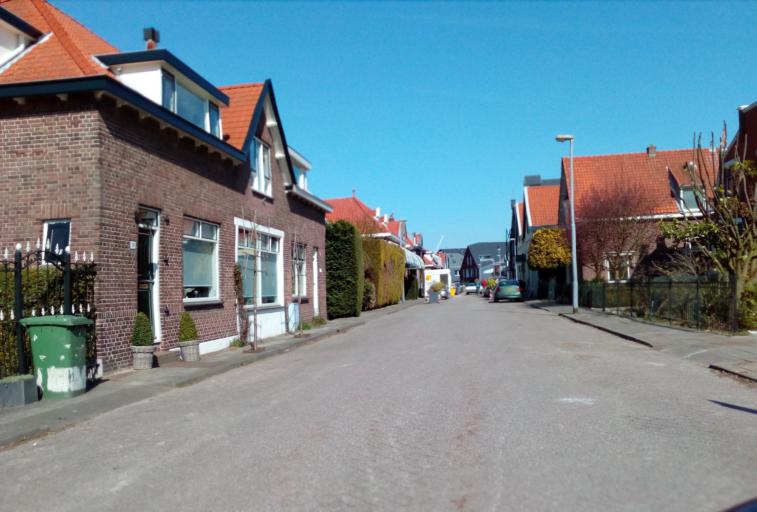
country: NL
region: South Holland
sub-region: Gemeente Lansingerland
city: Bergschenhoek
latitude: 51.9539
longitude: 4.5156
